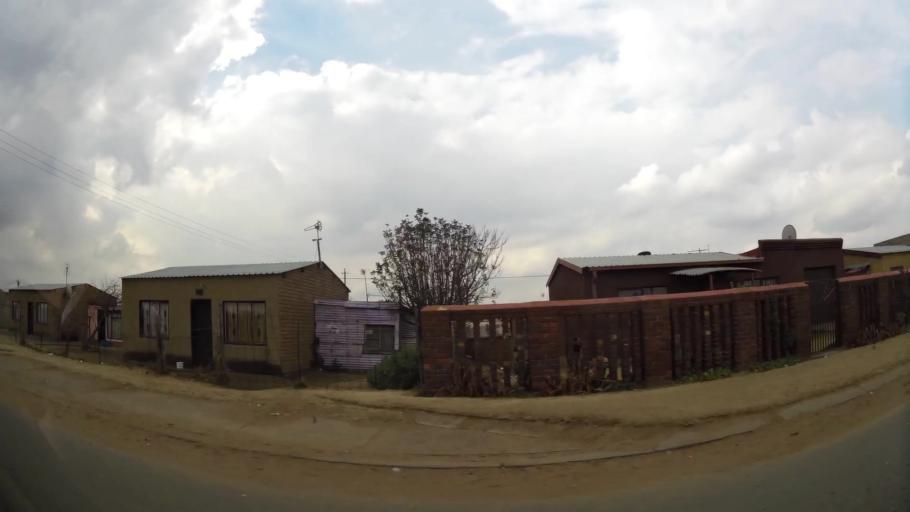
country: ZA
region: Orange Free State
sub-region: Fezile Dabi District Municipality
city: Sasolburg
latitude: -26.8596
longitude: 27.8814
